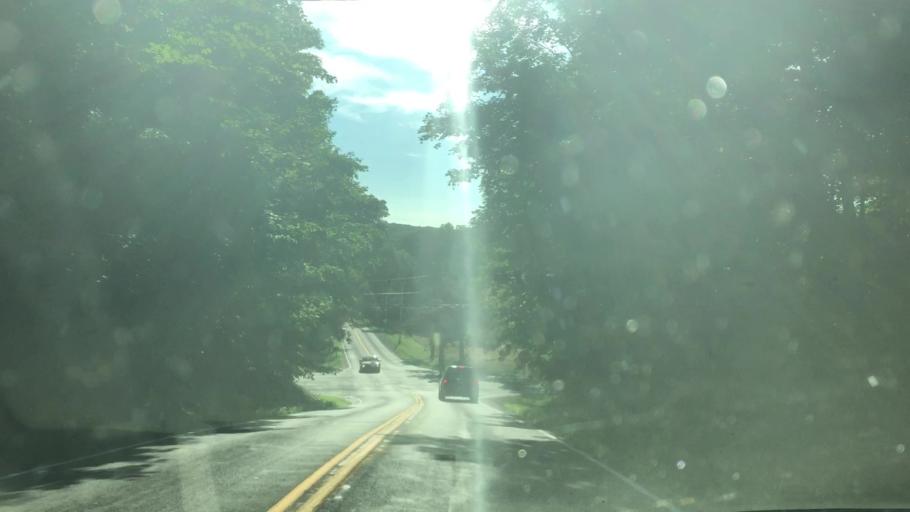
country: US
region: New York
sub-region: Ontario County
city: Victor
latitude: 43.0456
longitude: -77.3807
